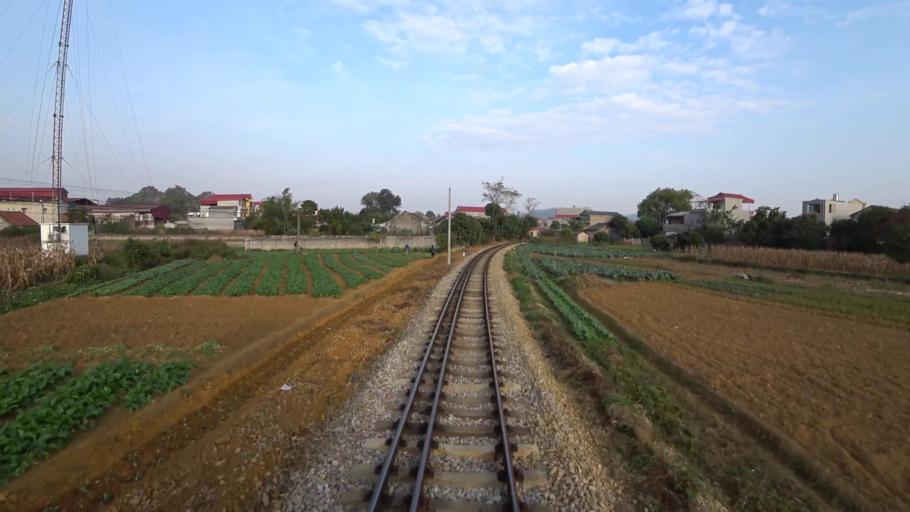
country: VN
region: Lang Son
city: Thi Tran Cao Loc
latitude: 21.8758
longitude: 106.7514
